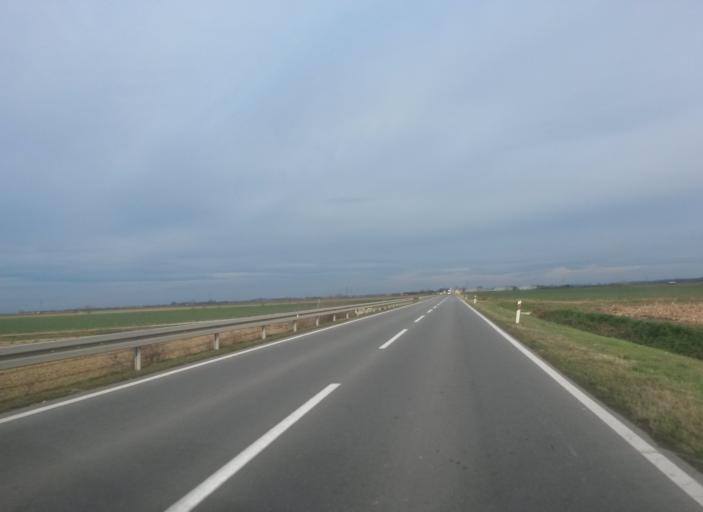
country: HR
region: Osjecko-Baranjska
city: Ovcara
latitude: 45.4826
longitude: 18.5426
